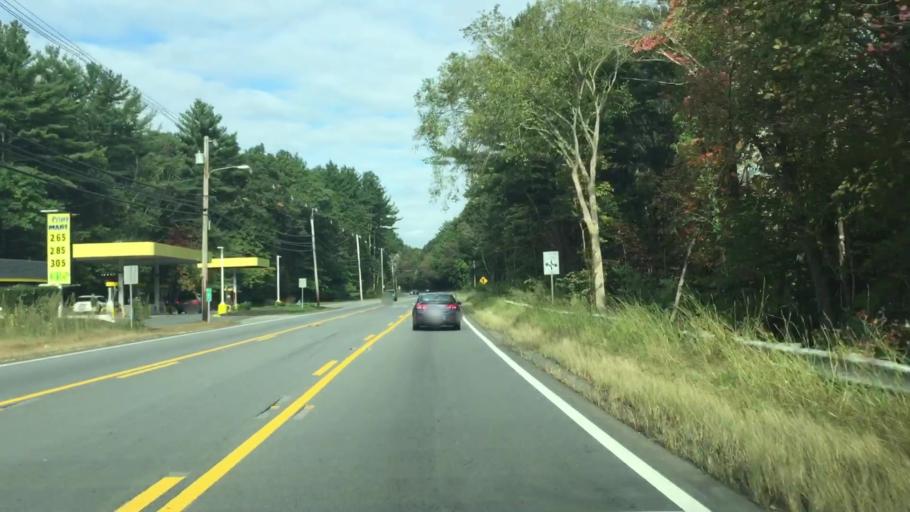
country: US
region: Massachusetts
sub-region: Essex County
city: Andover
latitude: 42.6376
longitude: -71.0784
